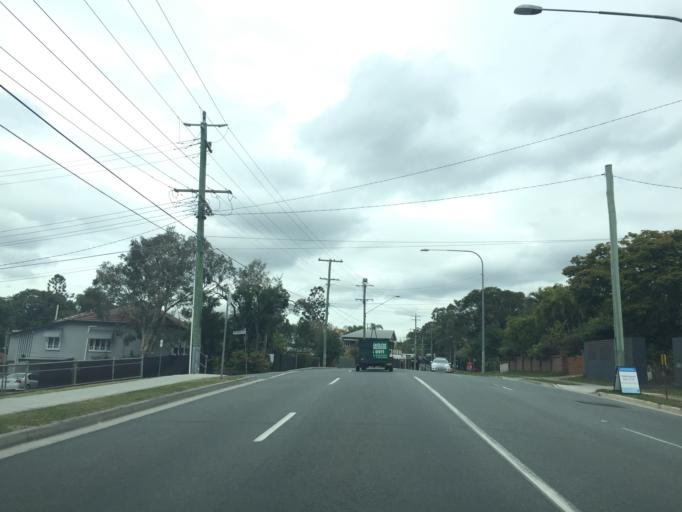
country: AU
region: Queensland
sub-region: Brisbane
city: Wilston
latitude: -27.4402
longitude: 152.9899
